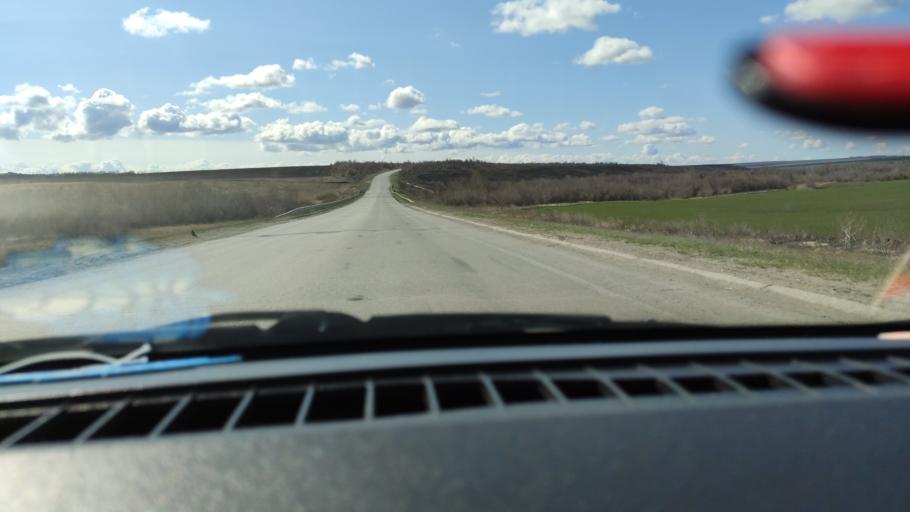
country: RU
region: Samara
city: Varlamovo
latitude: 53.0692
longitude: 48.3537
